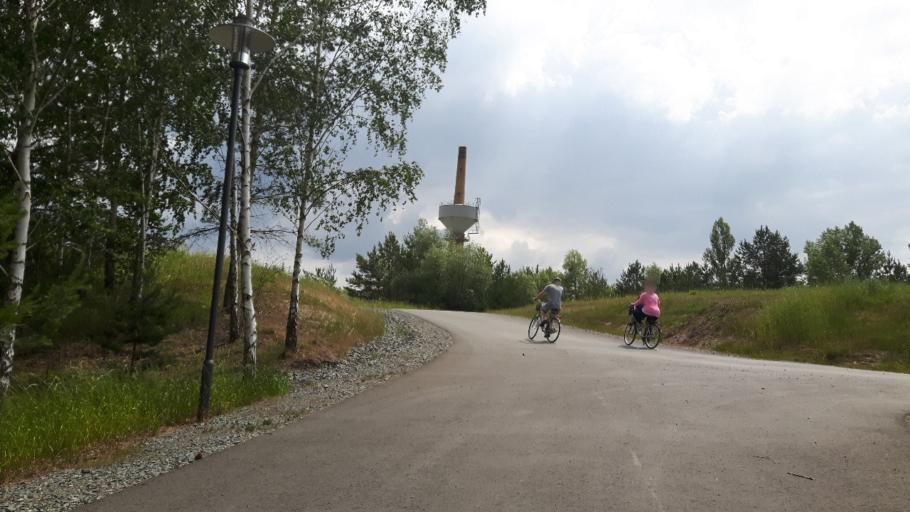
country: DE
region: Saxony-Anhalt
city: Grafenhainichen
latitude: 51.6955
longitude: 12.4552
